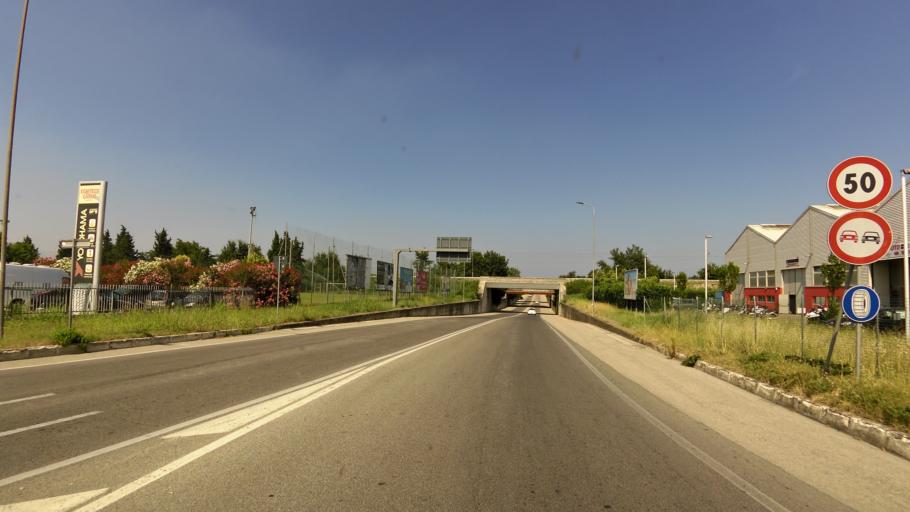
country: IT
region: Emilia-Romagna
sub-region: Provincia di Ravenna
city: Ravenna
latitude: 44.4010
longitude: 12.2147
